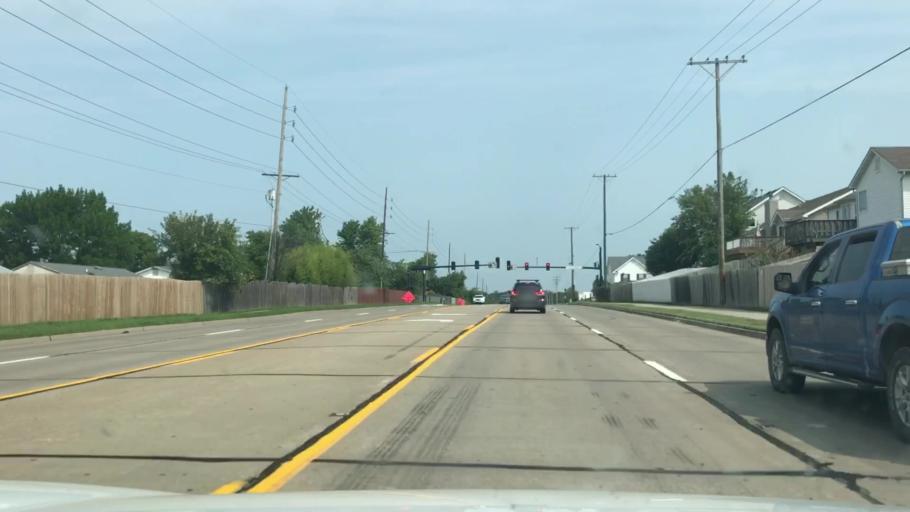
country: US
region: Missouri
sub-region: Saint Charles County
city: Dardenne Prairie
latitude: 38.7834
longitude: -90.7371
